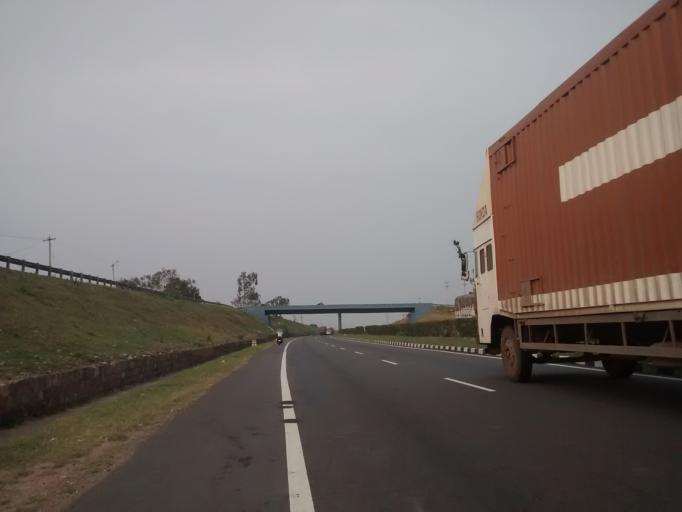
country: IN
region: Tamil Nadu
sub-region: Dharmapuri
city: Dharmapuri
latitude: 12.0905
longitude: 78.1141
